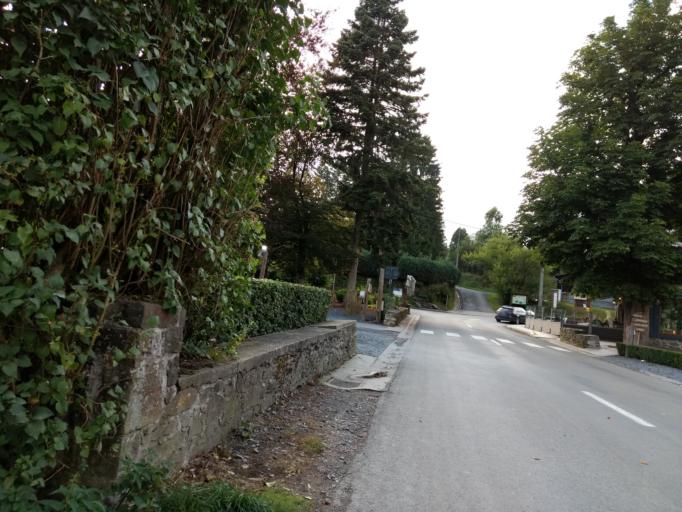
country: BE
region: Wallonia
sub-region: Province du Luxembourg
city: Houffalize
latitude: 50.1497
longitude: 5.7457
